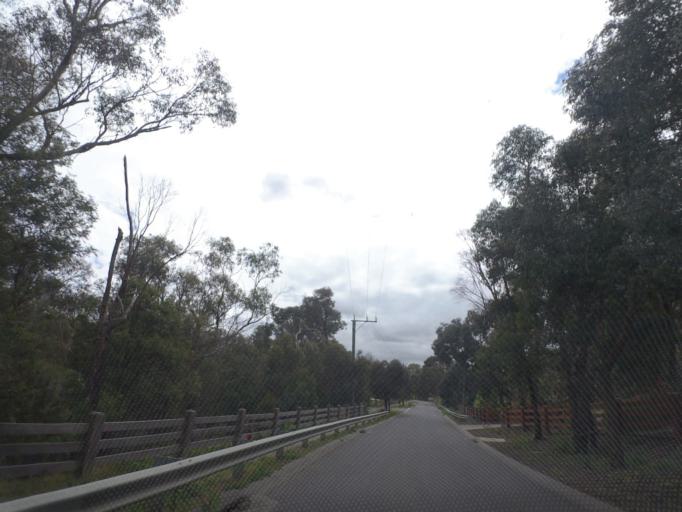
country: AU
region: Victoria
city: Plenty
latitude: -37.6656
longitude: 145.1195
